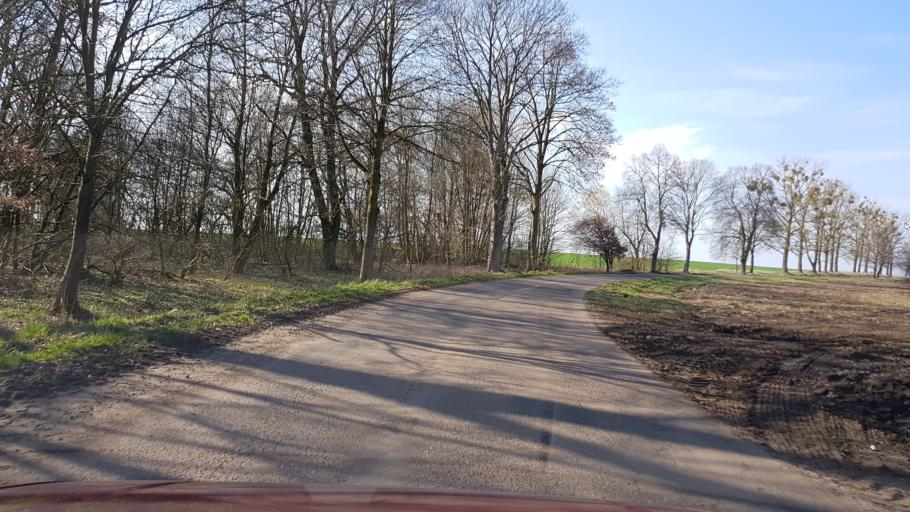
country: PL
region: West Pomeranian Voivodeship
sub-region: Powiat gryficki
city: Ploty
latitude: 53.7099
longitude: 15.2646
